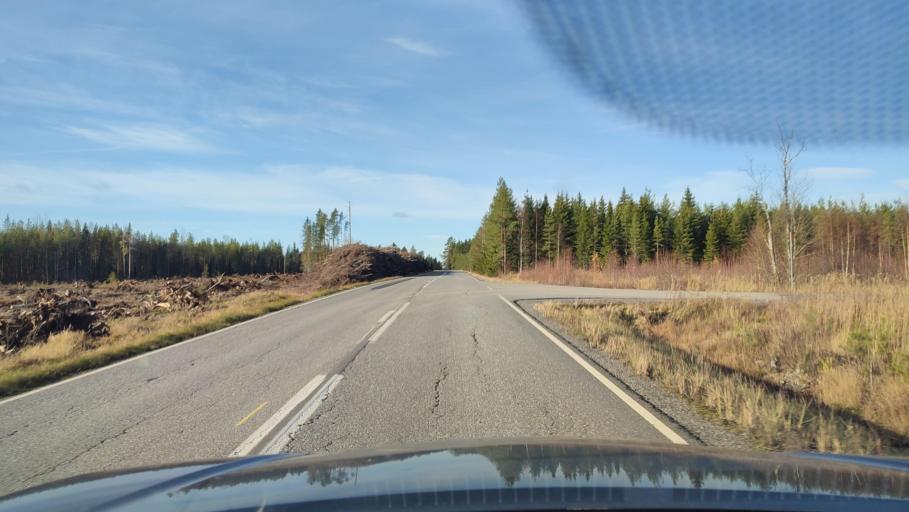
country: FI
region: Ostrobothnia
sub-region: Sydosterbotten
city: Naerpes
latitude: 62.4629
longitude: 21.5225
